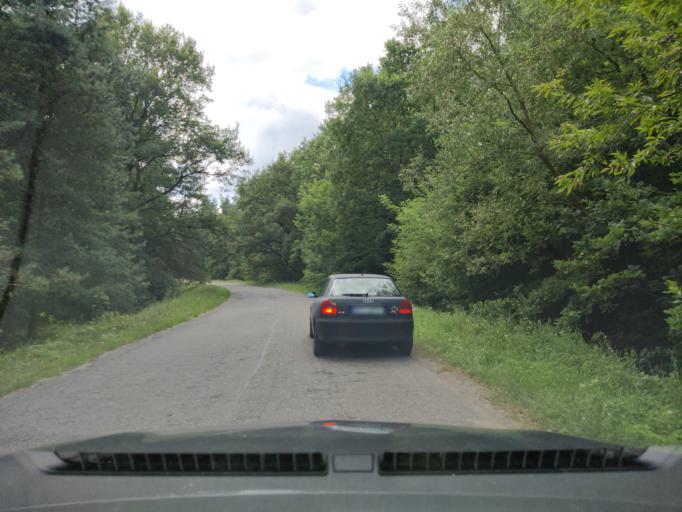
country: PL
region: Masovian Voivodeship
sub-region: Powiat pultuski
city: Pultusk
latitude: 52.7103
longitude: 21.1136
